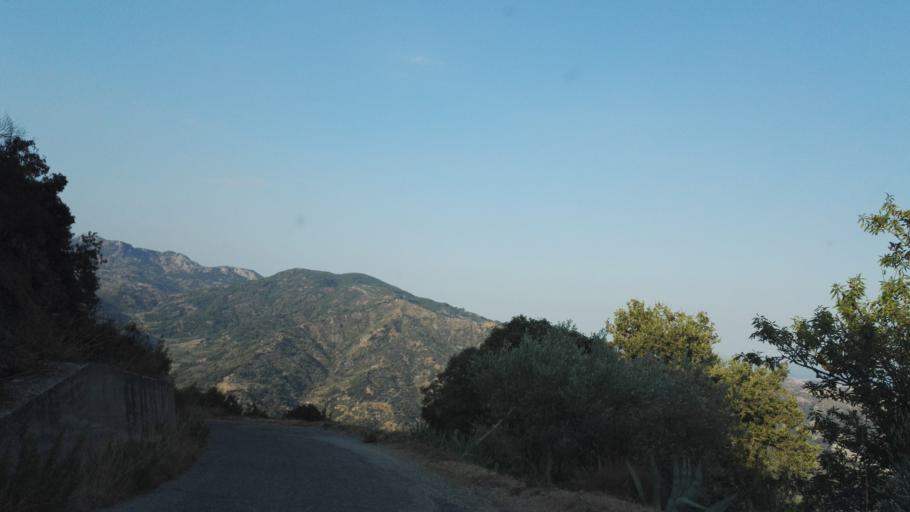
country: IT
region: Calabria
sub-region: Provincia di Reggio Calabria
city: Caulonia
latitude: 38.4075
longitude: 16.3615
